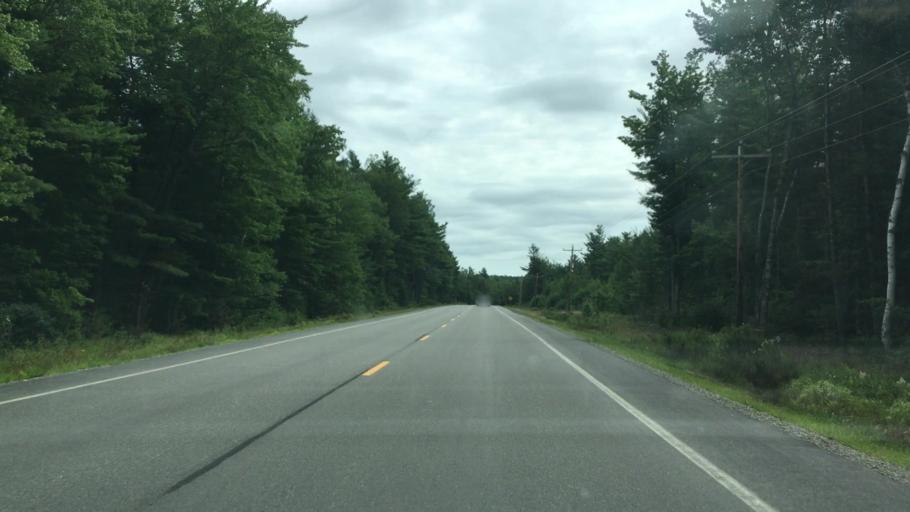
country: US
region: Maine
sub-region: Washington County
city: Machias
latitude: 45.0010
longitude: -67.5762
